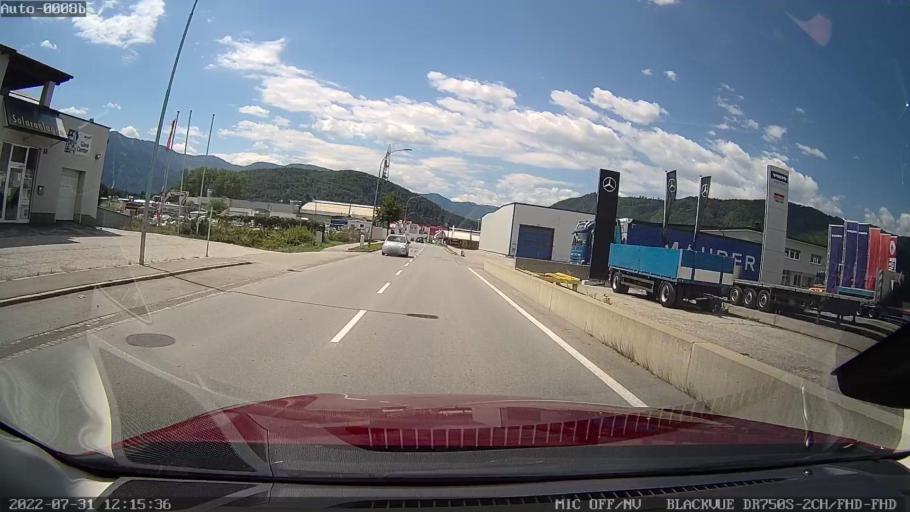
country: AT
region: Carinthia
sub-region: Villach Stadt
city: Villach
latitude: 46.5922
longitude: 13.8405
